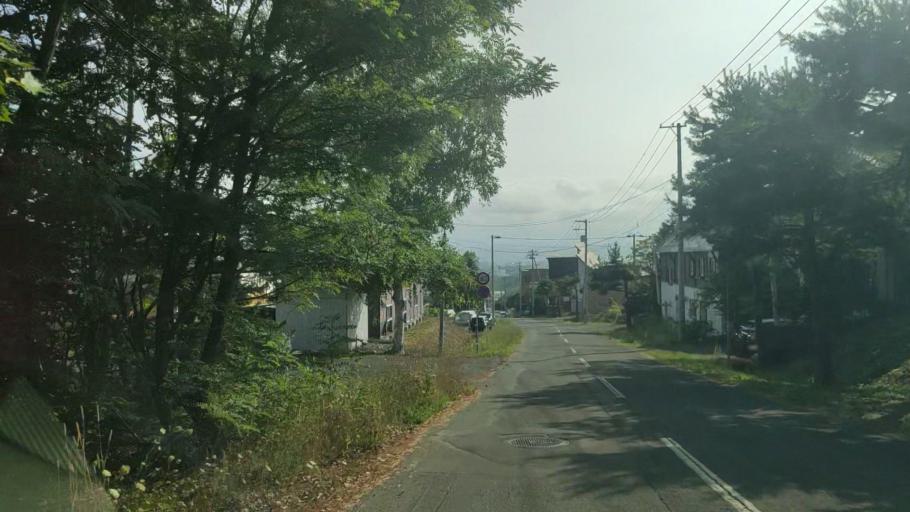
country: JP
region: Hokkaido
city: Shimo-furano
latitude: 43.3451
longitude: 142.3620
